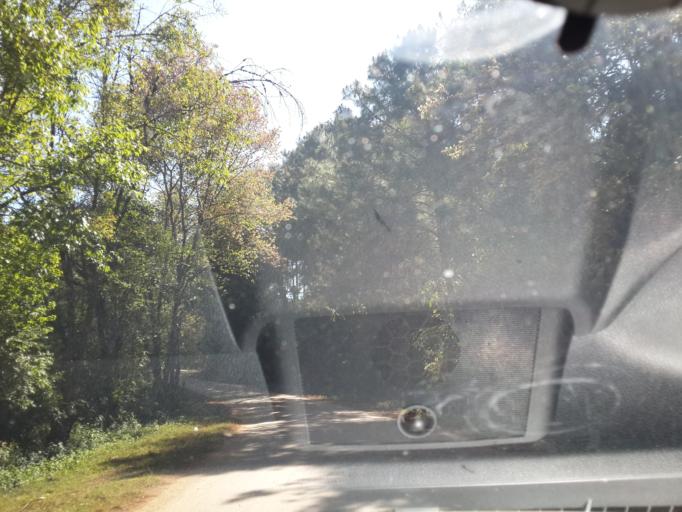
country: TH
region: Chiang Mai
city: Fang
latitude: 19.9302
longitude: 99.0419
